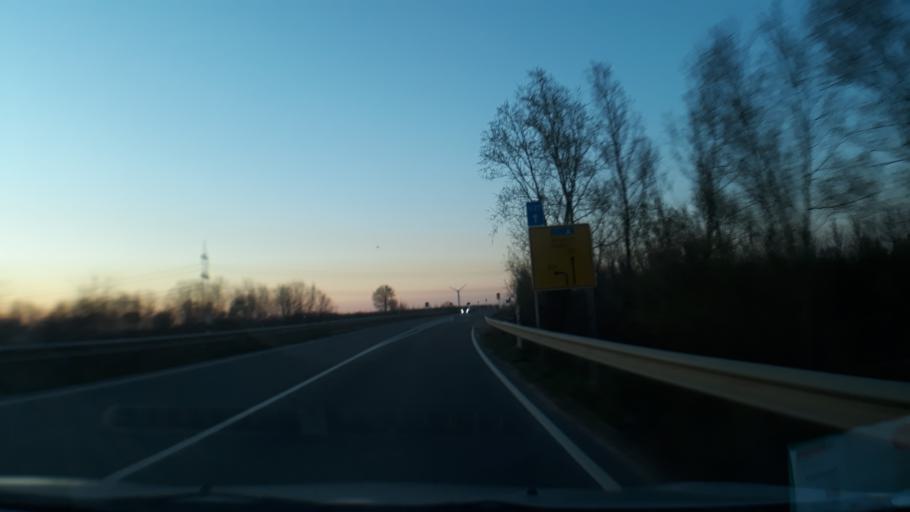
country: DE
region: North Rhine-Westphalia
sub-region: Regierungsbezirk Koln
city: Norvenich
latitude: 50.8522
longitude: 6.6135
